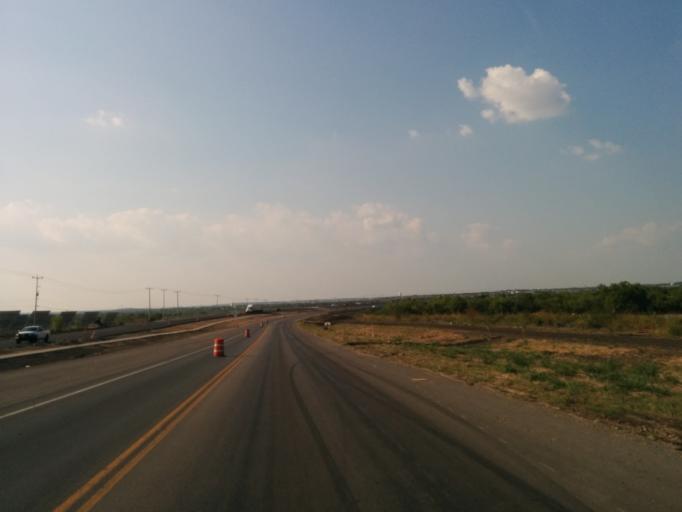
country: US
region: Texas
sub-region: Bexar County
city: Converse
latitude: 29.4774
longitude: -98.2955
